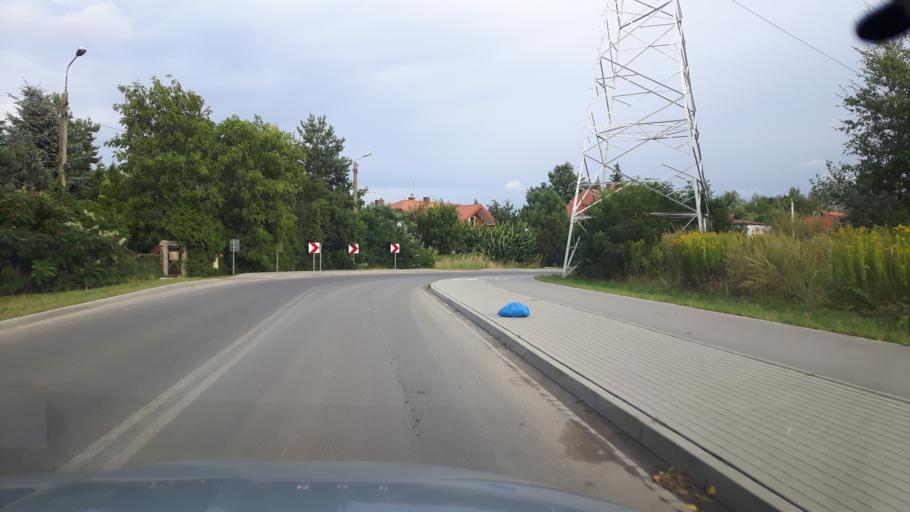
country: PL
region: Masovian Voivodeship
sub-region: Powiat wolominski
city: Marki
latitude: 52.3290
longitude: 21.1265
